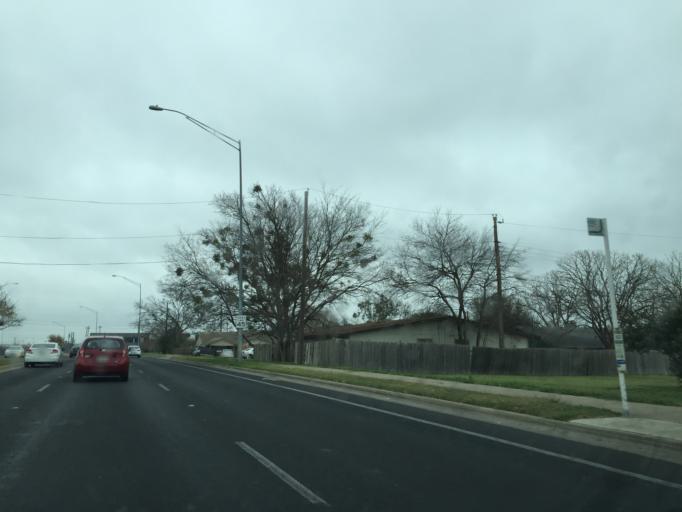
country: US
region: Texas
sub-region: Travis County
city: Wells Branch
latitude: 30.3858
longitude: -97.6952
